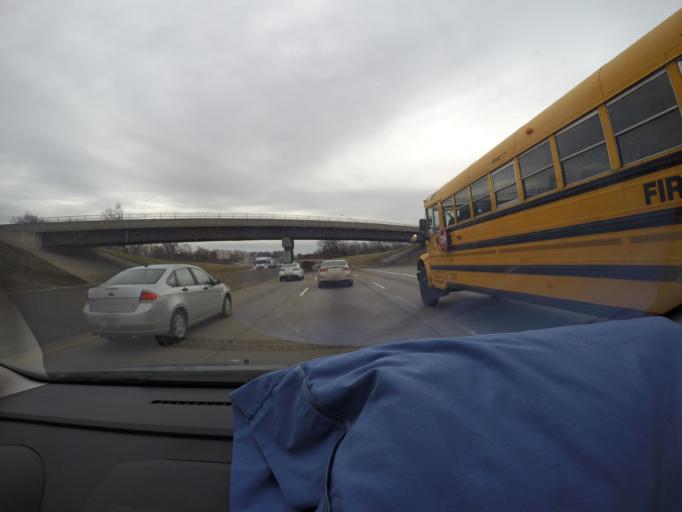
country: US
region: Missouri
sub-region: Saint Louis County
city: Normandy
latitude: 38.7171
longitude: -90.2982
